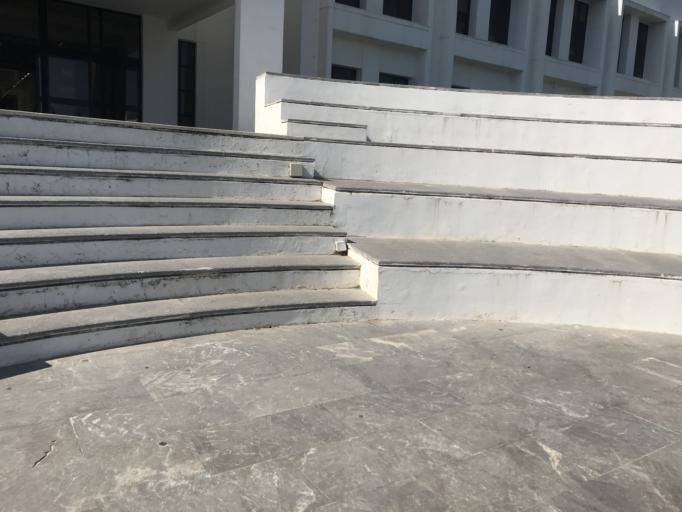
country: GR
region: Crete
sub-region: Nomos Irakleiou
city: Gazi
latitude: 35.3052
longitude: 25.0727
